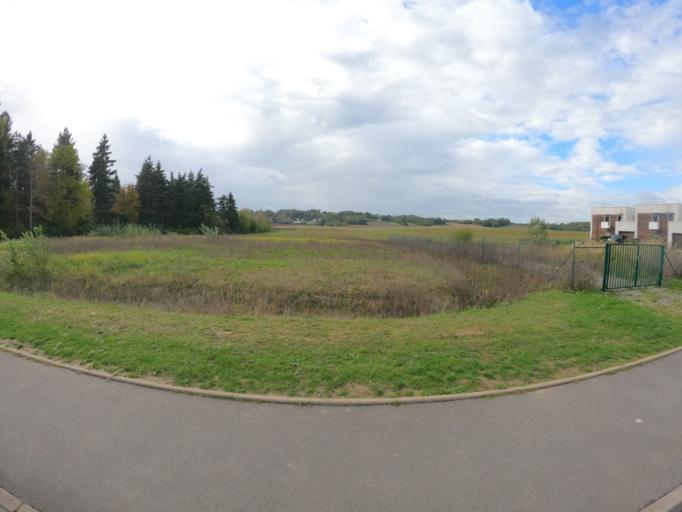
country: FR
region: Ile-de-France
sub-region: Departement de Seine-et-Marne
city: Saint-Germain-sur-Morin
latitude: 48.8826
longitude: 2.8439
